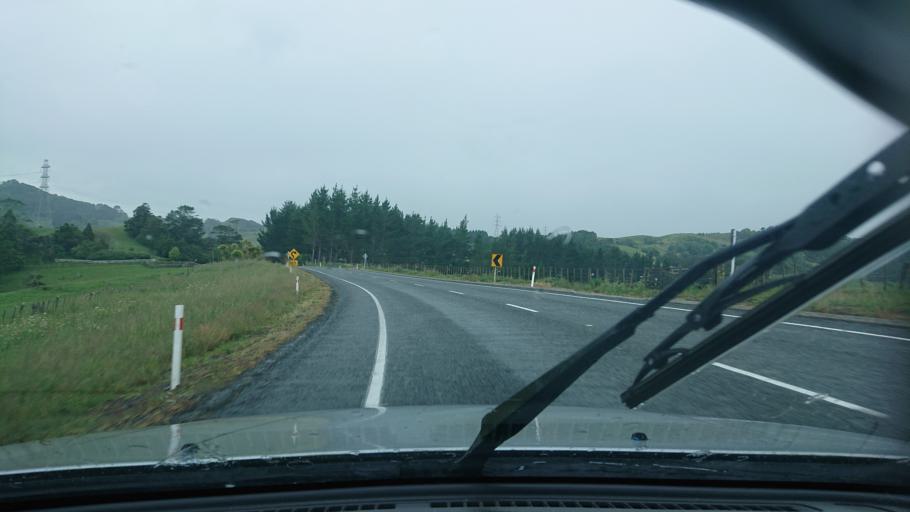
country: NZ
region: Auckland
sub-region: Auckland
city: Wellsford
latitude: -36.3383
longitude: 174.4696
